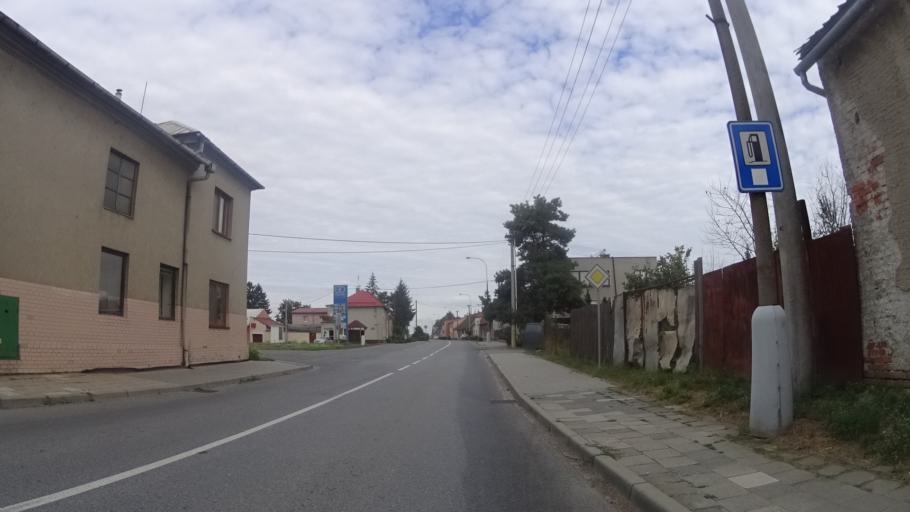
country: CZ
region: Olomoucky
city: Tovacov
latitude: 49.4367
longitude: 17.2847
